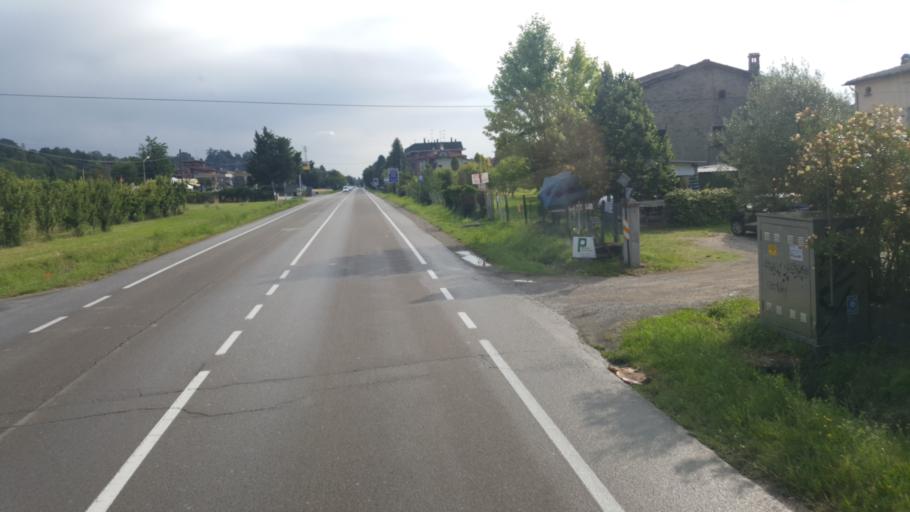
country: IT
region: Emilia-Romagna
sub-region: Provincia di Modena
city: Vignola
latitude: 44.4741
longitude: 10.9869
